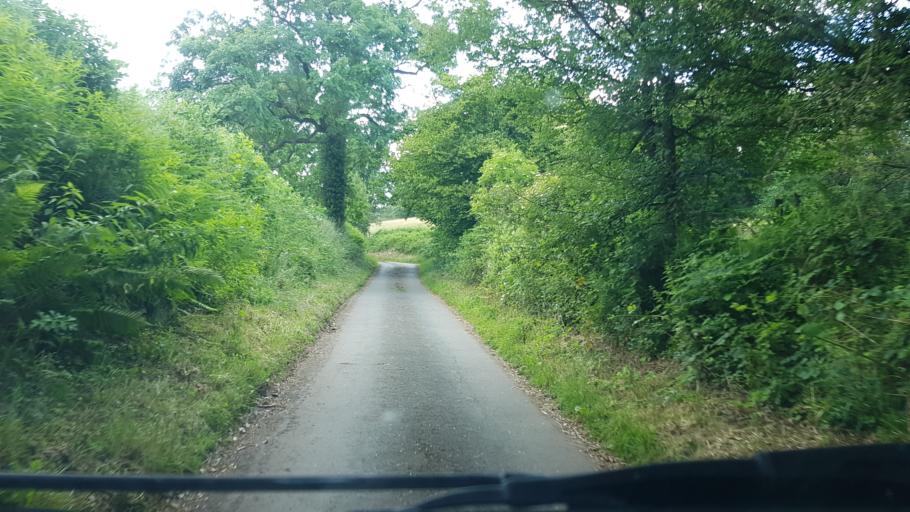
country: GB
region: England
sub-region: Shropshire
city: Romsley
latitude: 52.4638
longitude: -2.2656
